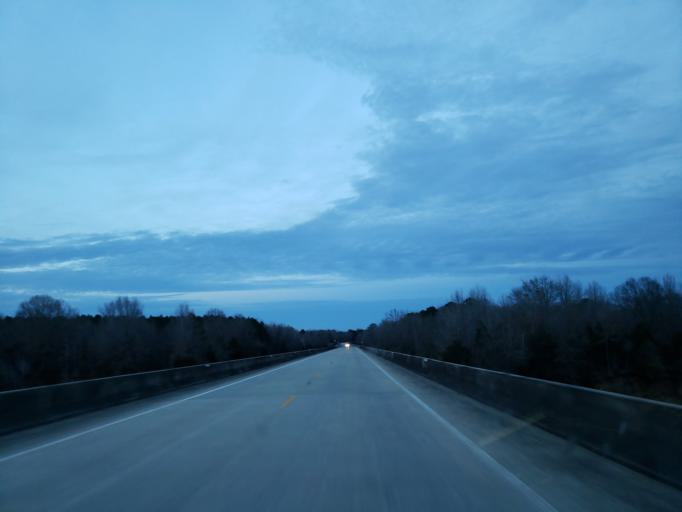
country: US
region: Alabama
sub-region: Sumter County
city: Livingston
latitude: 32.8251
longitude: -88.1564
